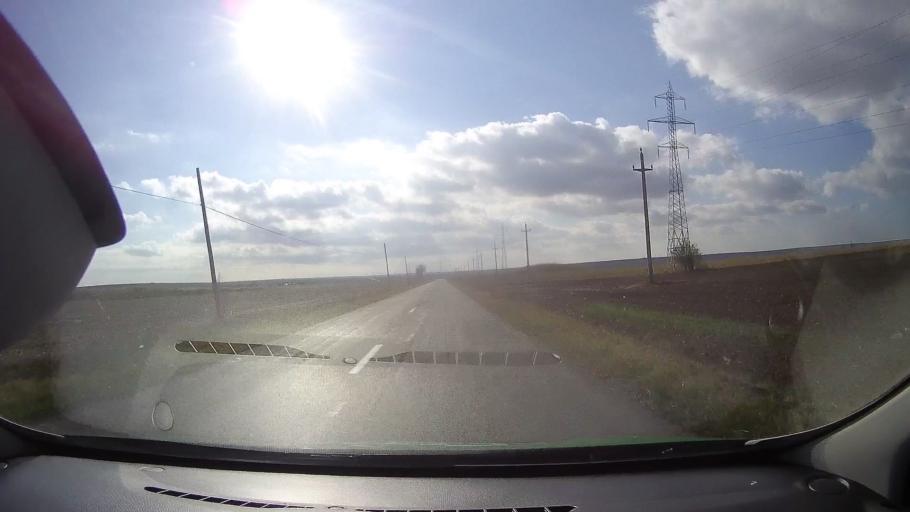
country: RO
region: Constanta
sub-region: Comuna Istria
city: Nuntasi
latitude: 44.5380
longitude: 28.6880
